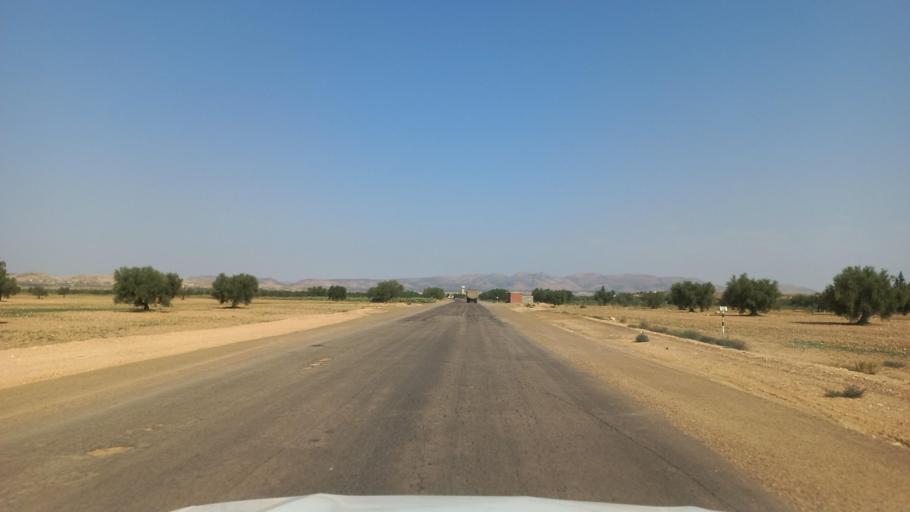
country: TN
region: Al Qasrayn
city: Sbiba
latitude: 35.3460
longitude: 9.0543
